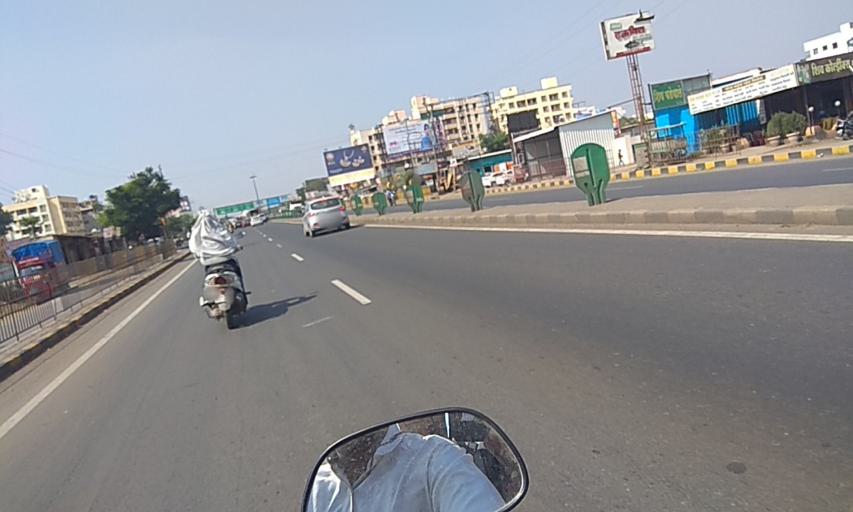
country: IN
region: Maharashtra
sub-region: Pune Division
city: Lohogaon
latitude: 18.4928
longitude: 73.9956
